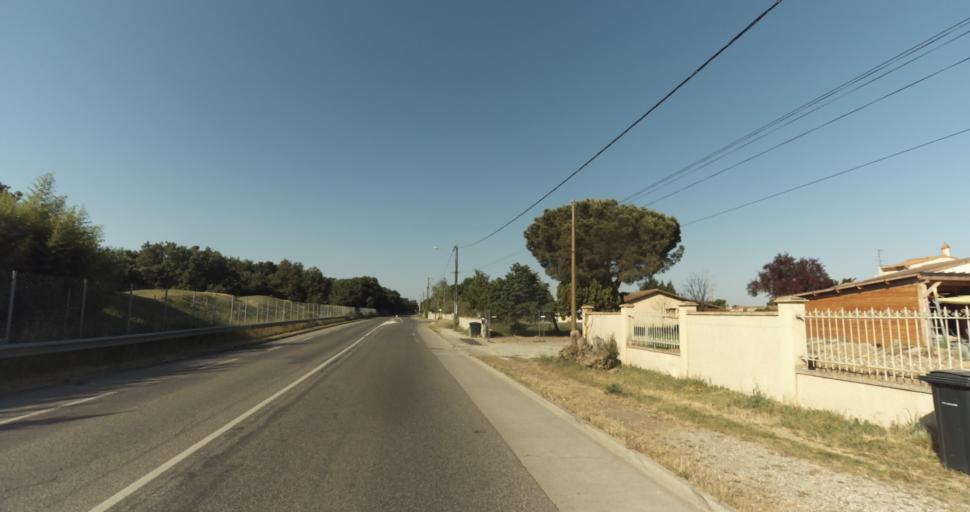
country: FR
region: Midi-Pyrenees
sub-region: Departement de la Haute-Garonne
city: La Salvetat-Saint-Gilles
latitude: 43.5600
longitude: 1.2620
